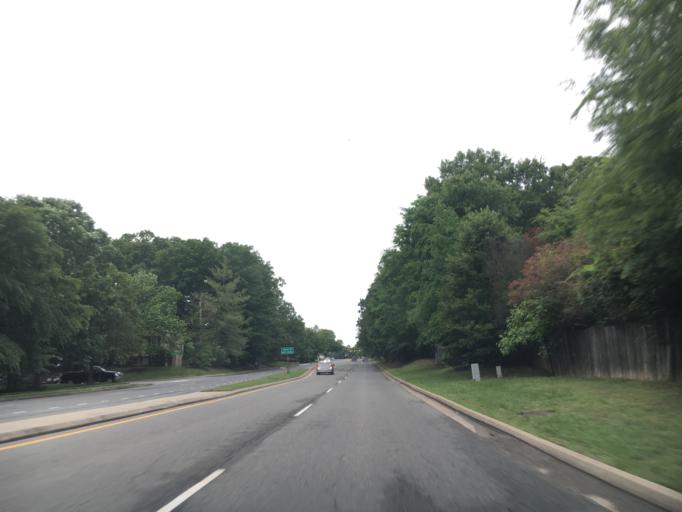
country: US
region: Virginia
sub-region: Henrico County
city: Short Pump
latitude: 37.6230
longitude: -77.6335
